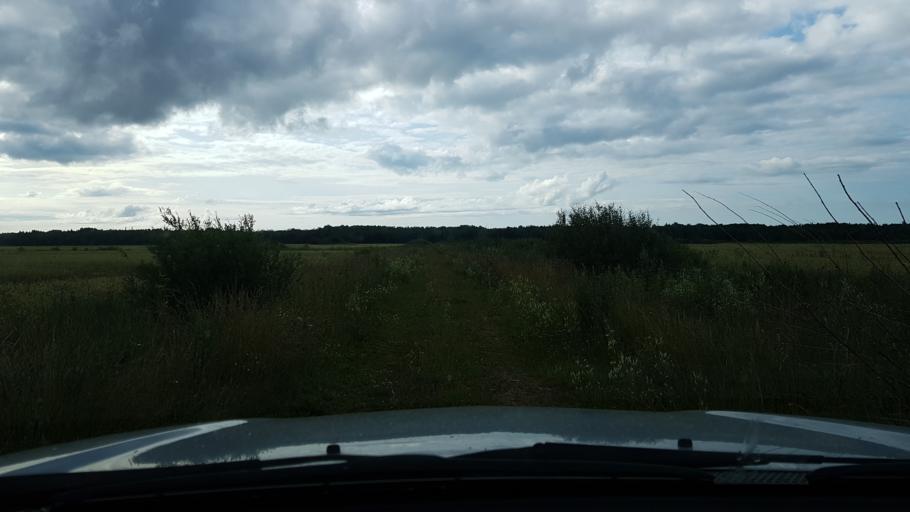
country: EE
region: Ida-Virumaa
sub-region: Narva-Joesuu linn
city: Narva-Joesuu
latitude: 59.3858
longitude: 27.9996
